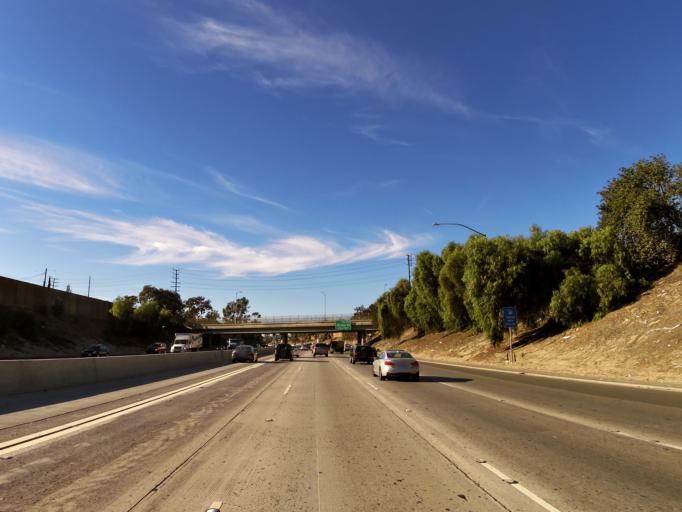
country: US
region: California
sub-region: Los Angeles County
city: North Hollywood
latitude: 34.2284
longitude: -118.3919
